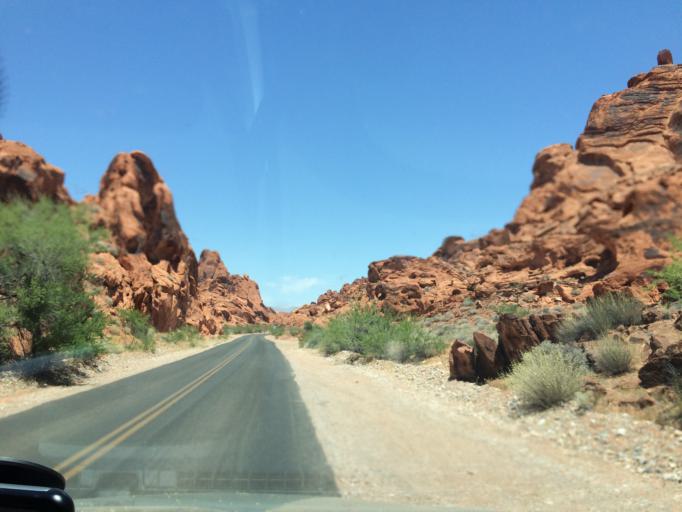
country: US
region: Nevada
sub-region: Clark County
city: Moapa Valley
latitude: 36.4368
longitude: -114.5175
